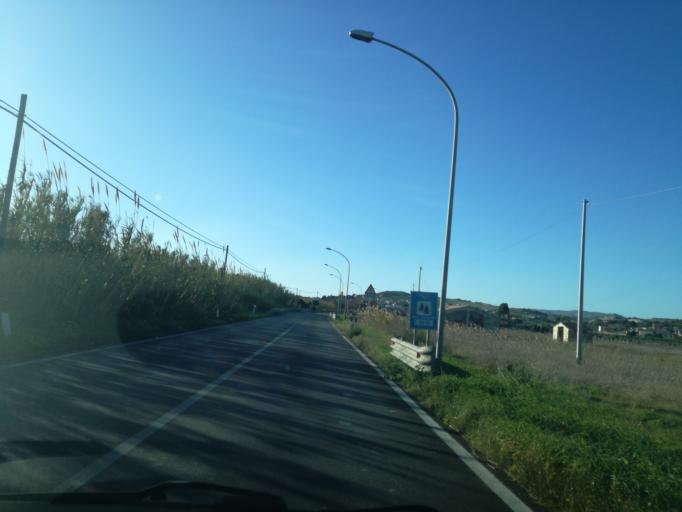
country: IT
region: Sicily
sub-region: Provincia di Caltanissetta
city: Gela
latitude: 37.0967
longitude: 14.1676
